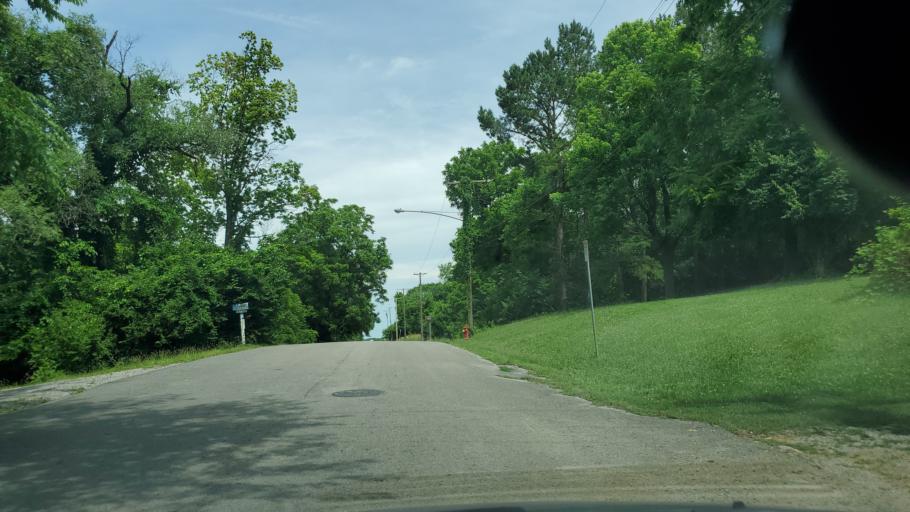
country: US
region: Tennessee
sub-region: Davidson County
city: Oak Hill
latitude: 36.1064
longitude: -86.6940
